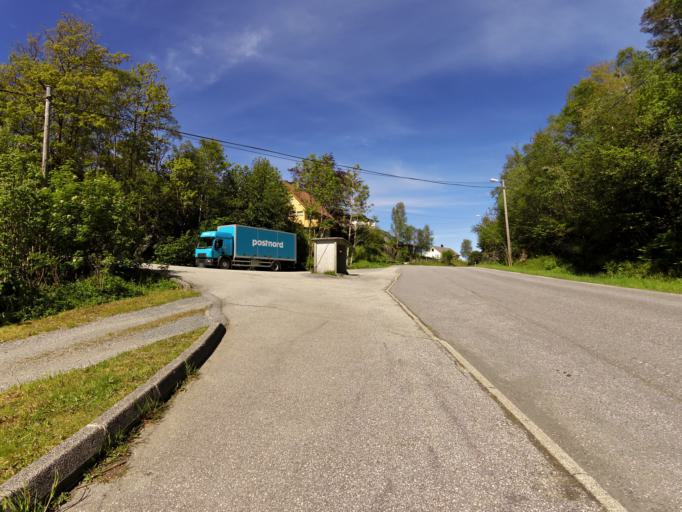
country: NO
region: Hordaland
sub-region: Stord
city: Sagvag
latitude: 59.7889
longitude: 5.4241
